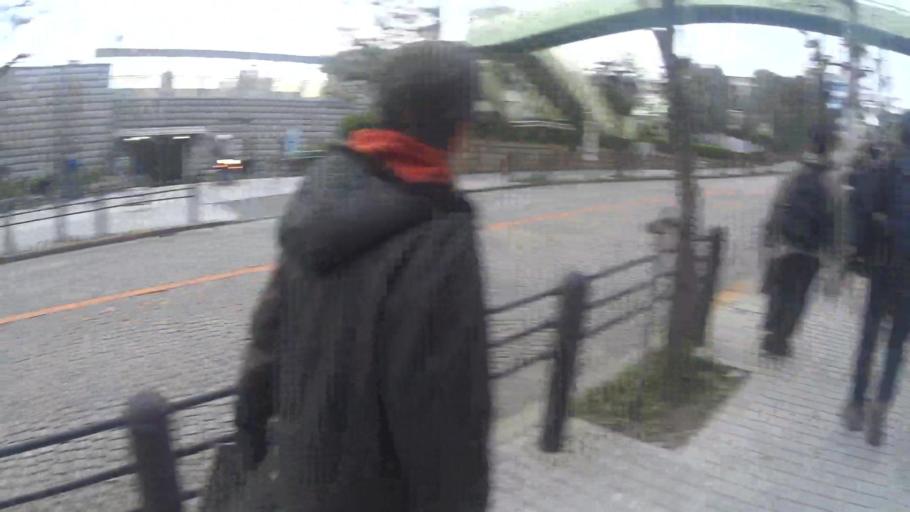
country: JP
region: Osaka
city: Osaka-shi
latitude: 34.6720
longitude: 135.5280
